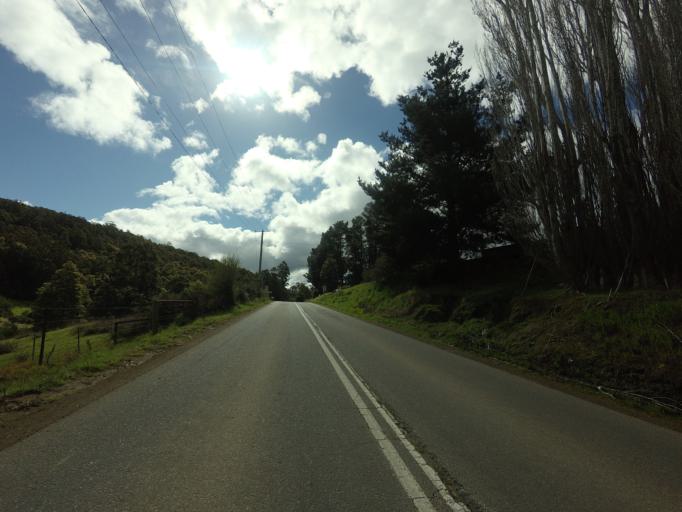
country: AU
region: Tasmania
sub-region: Huon Valley
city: Geeveston
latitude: -43.2379
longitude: 146.9912
